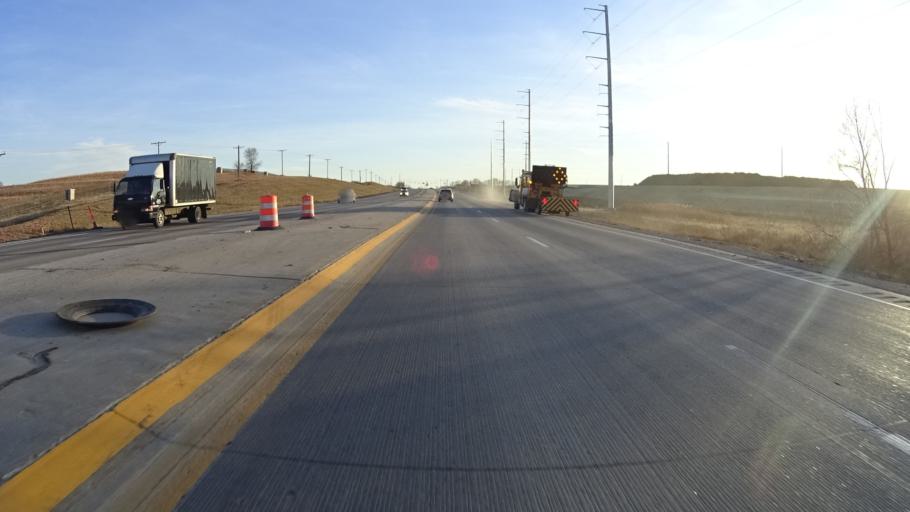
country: US
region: Nebraska
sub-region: Sarpy County
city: Chalco
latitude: 41.1379
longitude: -96.1391
